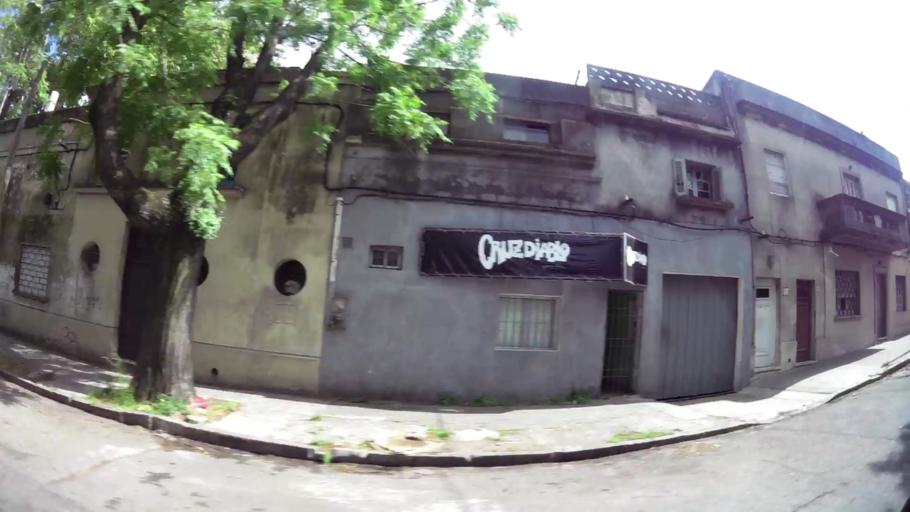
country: UY
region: Montevideo
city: Montevideo
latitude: -34.8796
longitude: -56.1758
